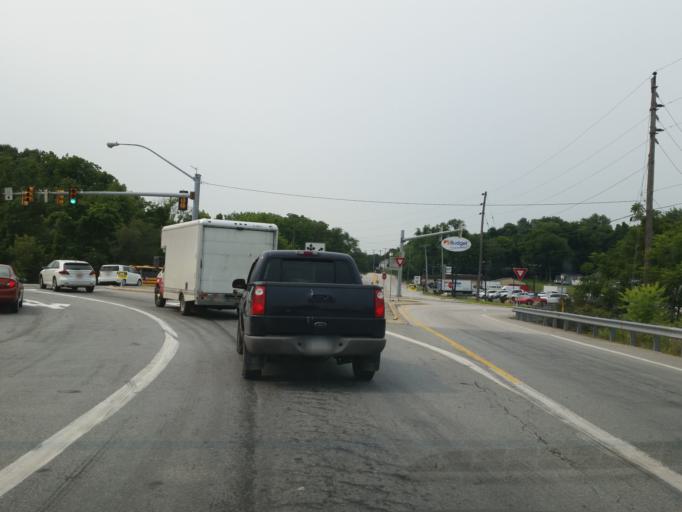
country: US
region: Pennsylvania
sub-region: York County
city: North York
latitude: 39.9913
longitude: -76.7354
